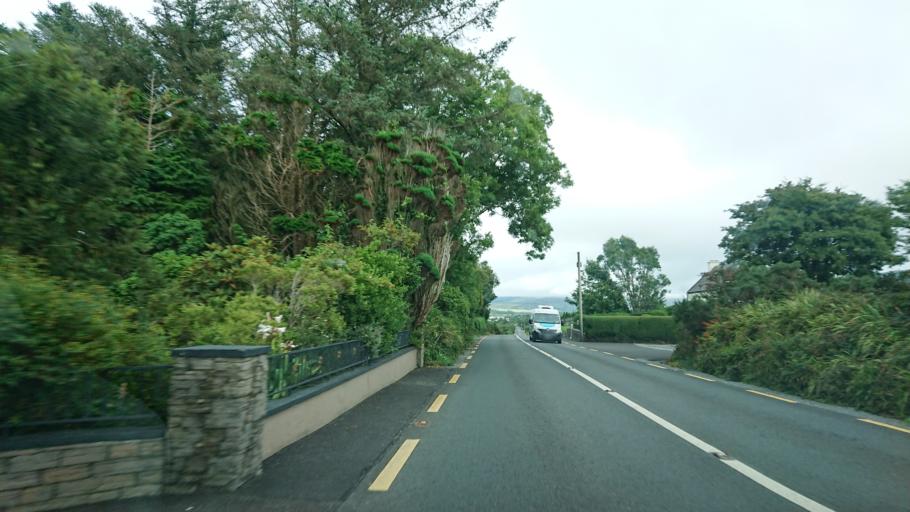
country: IE
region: Munster
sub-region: Ciarrai
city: Cahersiveen
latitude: 51.9573
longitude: -10.1922
